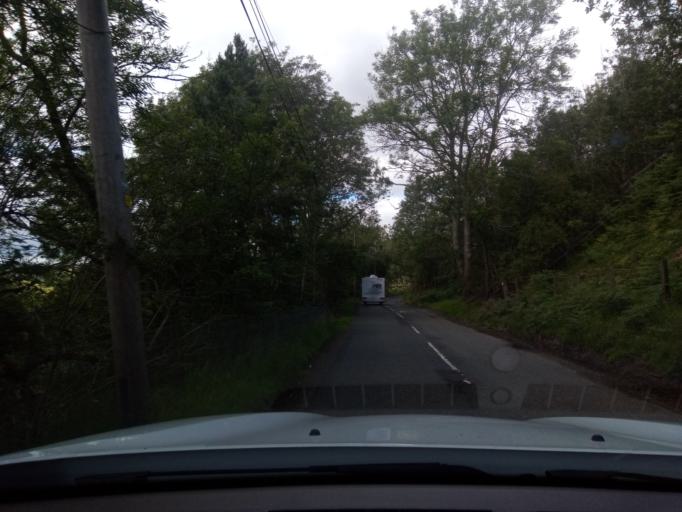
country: GB
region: Scotland
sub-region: The Scottish Borders
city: Innerleithen
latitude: 55.5392
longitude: -3.0070
